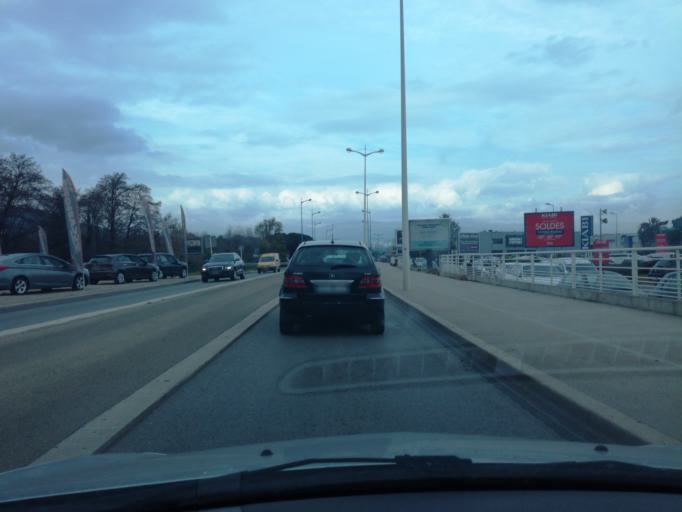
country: FR
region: Provence-Alpes-Cote d'Azur
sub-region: Departement des Alpes-Maritimes
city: Mandelieu-la-Napoule
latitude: 43.5520
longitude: 6.9555
